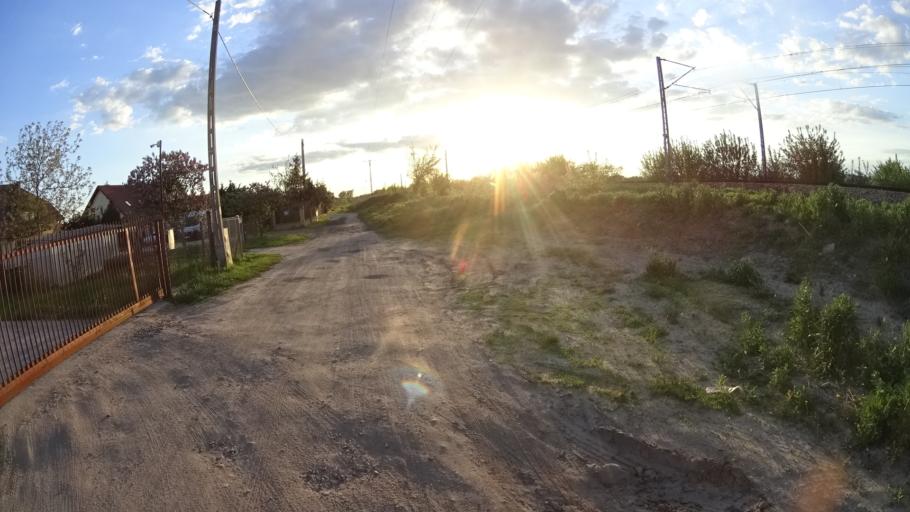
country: PL
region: Masovian Voivodeship
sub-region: Powiat pruszkowski
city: Piastow
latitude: 52.2063
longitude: 20.8337
